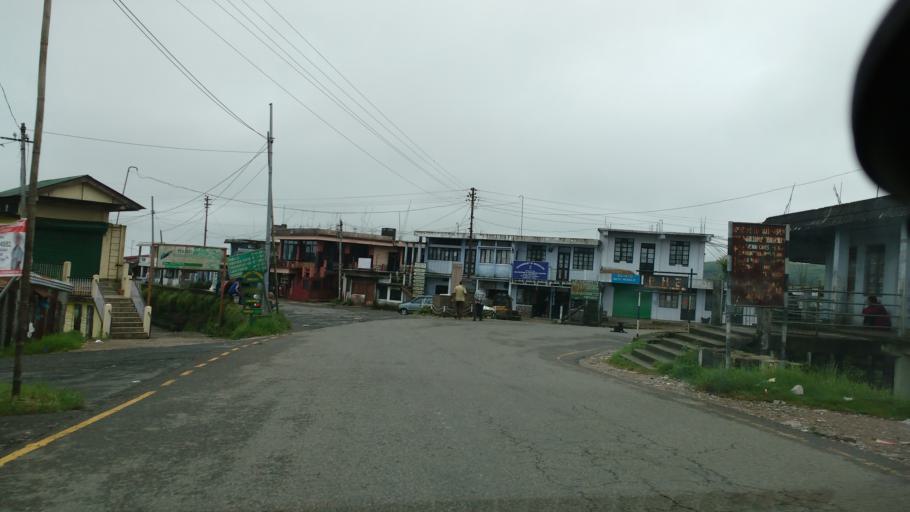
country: IN
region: Meghalaya
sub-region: East Khasi Hills
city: Cherrapunji
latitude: 25.2707
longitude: 91.7326
